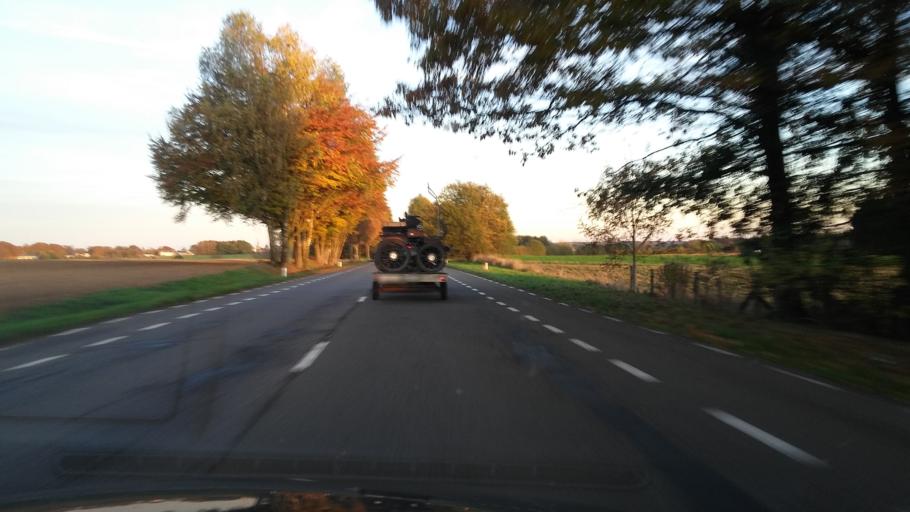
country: BE
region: Wallonia
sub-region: Province du Luxembourg
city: Florenville
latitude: 49.6989
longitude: 5.2809
